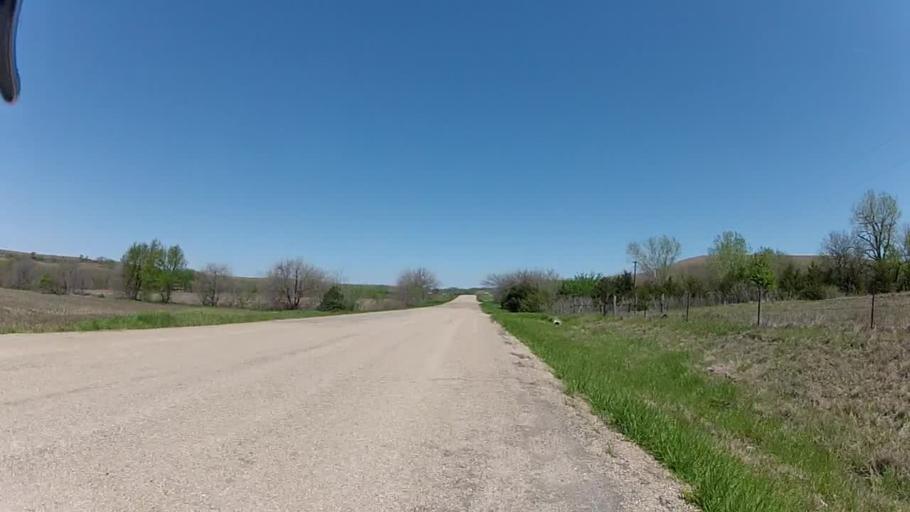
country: US
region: Kansas
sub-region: Riley County
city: Ogden
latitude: 38.9809
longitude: -96.5890
